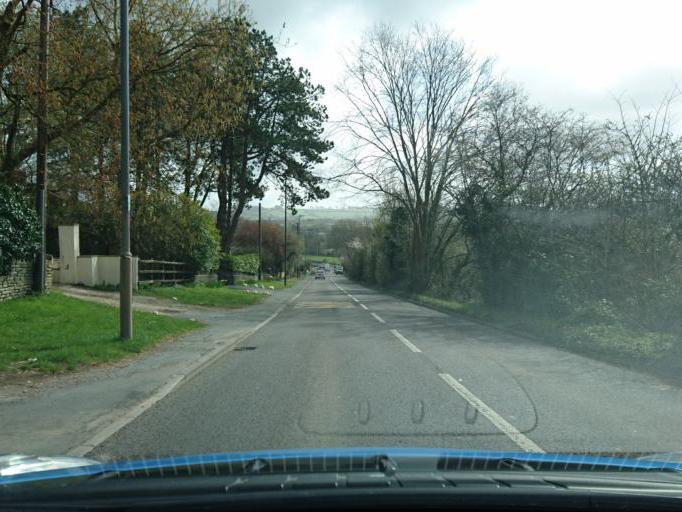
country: GB
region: England
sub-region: South Gloucestershire
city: Siston
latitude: 51.4529
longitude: -2.4446
